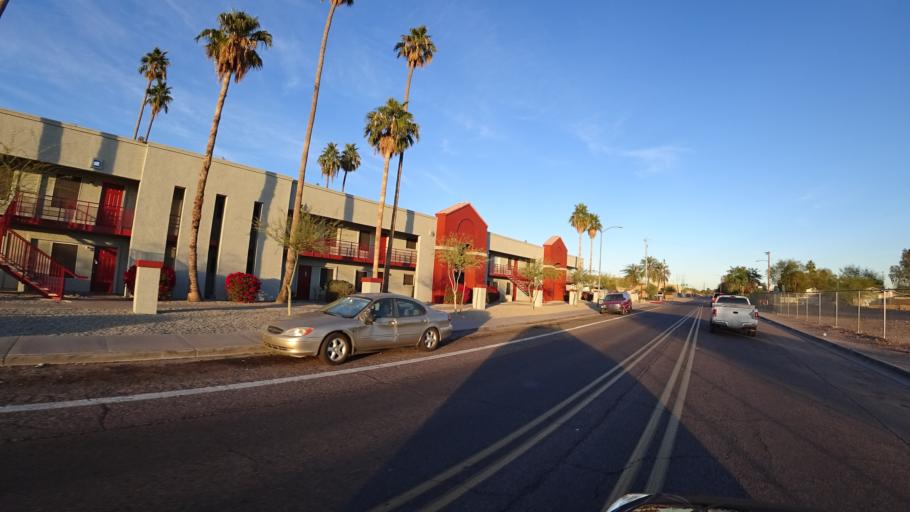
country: US
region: Arizona
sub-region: Maricopa County
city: Phoenix
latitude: 33.4585
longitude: -112.0117
